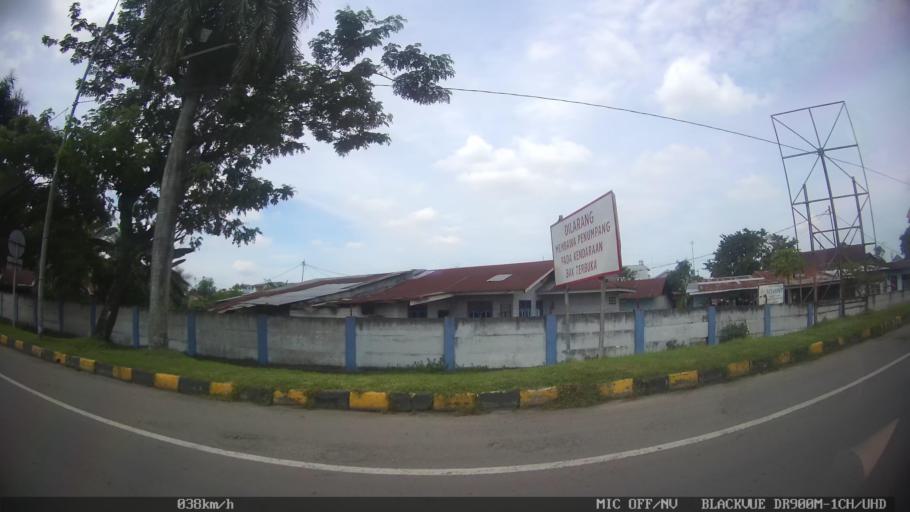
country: ID
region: North Sumatra
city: Medan
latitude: 3.6448
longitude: 98.6807
